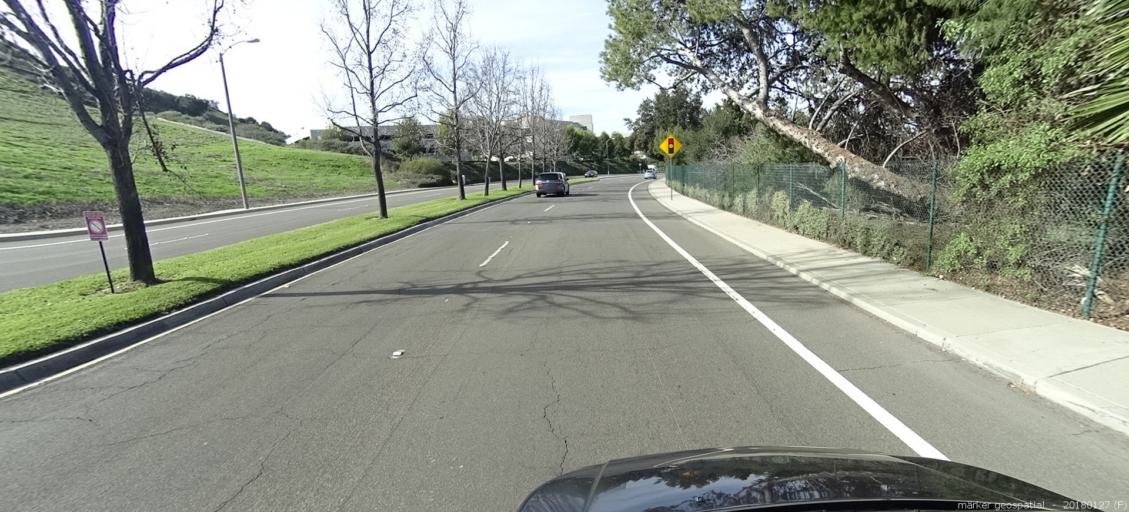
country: US
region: California
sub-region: Los Angeles County
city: Diamond Bar
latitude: 34.0029
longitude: -117.8260
